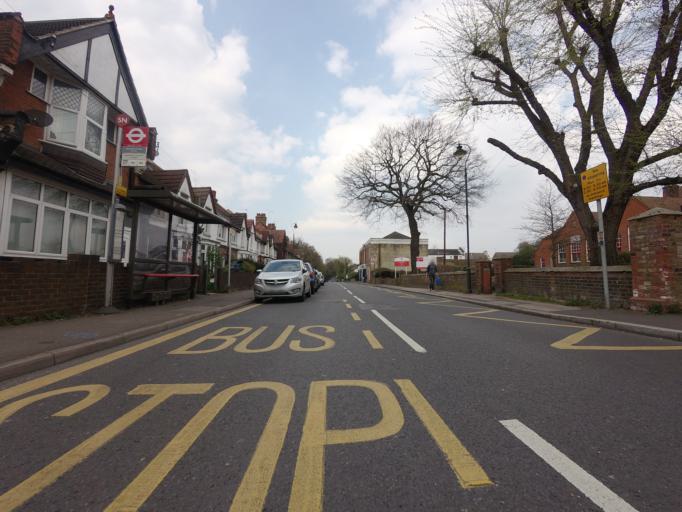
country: GB
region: England
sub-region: Greater London
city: Orpington
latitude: 51.3870
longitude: 0.1136
